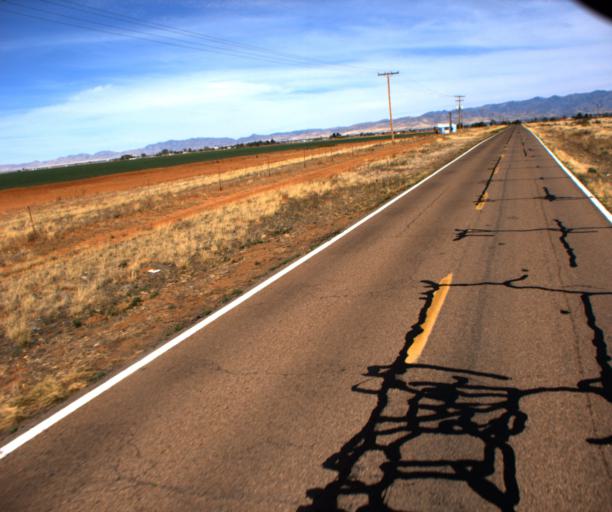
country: US
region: Arizona
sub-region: Cochise County
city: Willcox
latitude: 31.8837
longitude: -109.6719
